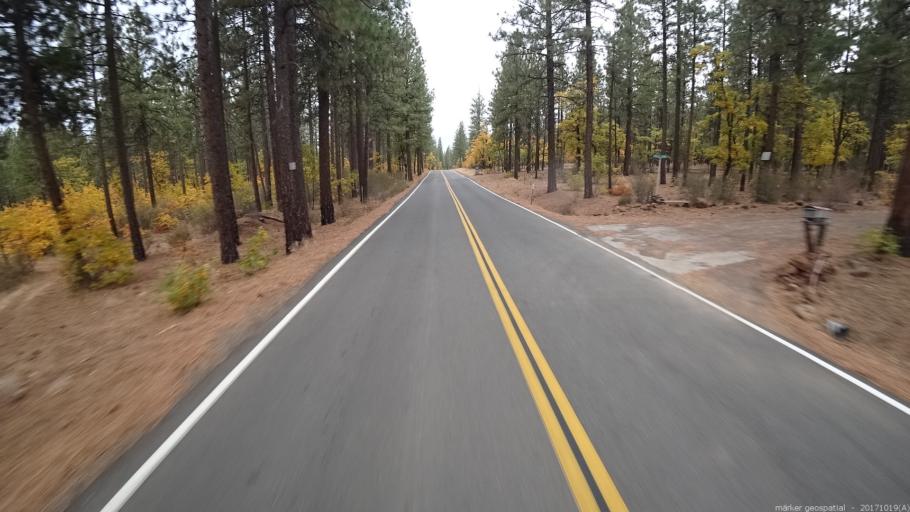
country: US
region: California
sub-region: Shasta County
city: Burney
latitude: 41.1684
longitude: -121.3595
